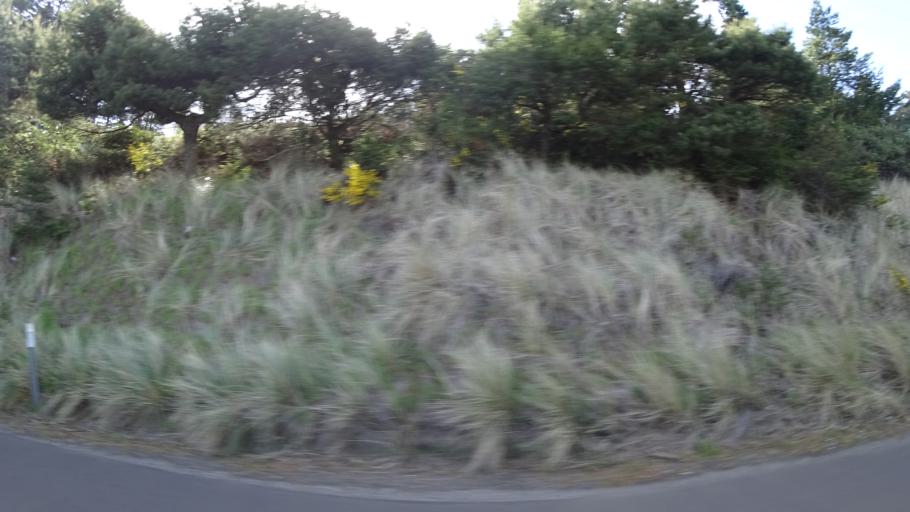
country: US
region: Oregon
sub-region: Lane County
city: Dunes City
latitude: 43.9015
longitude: -124.1160
